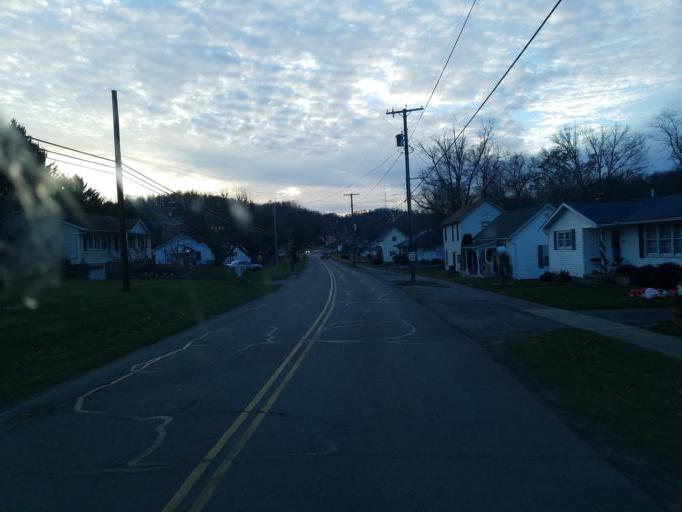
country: US
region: Ohio
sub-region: Muskingum County
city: Dresden
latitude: 40.1249
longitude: -82.0172
